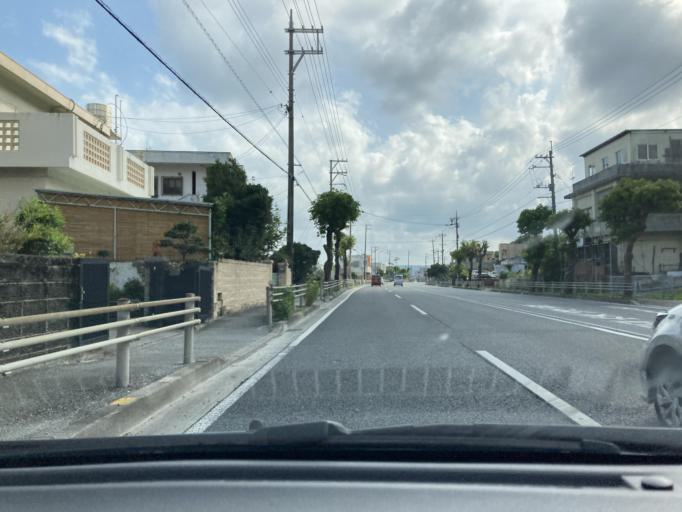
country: JP
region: Okinawa
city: Ginowan
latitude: 26.2471
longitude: 127.7819
